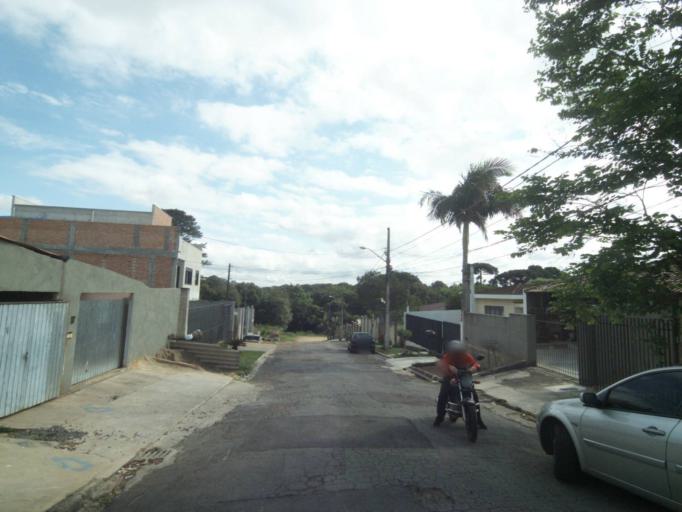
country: BR
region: Parana
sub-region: Curitiba
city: Curitiba
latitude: -25.3817
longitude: -49.2974
